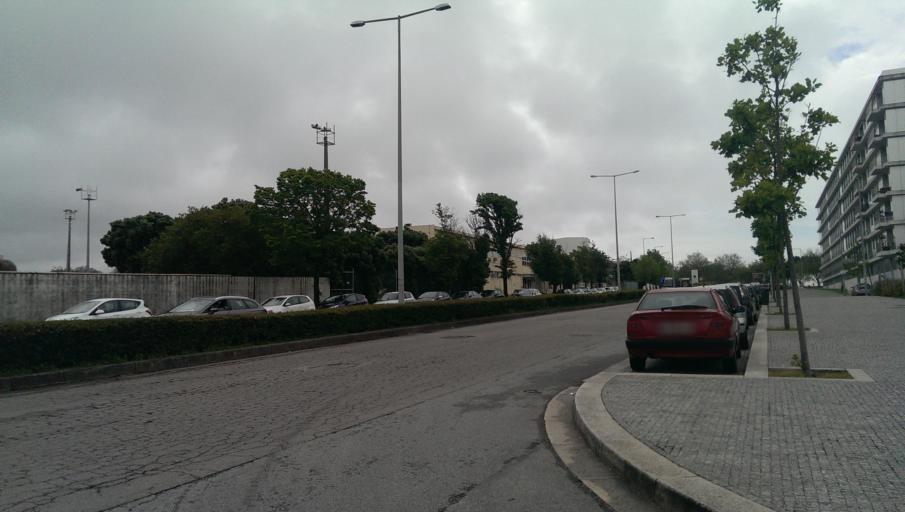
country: PT
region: Porto
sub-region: Matosinhos
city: Matosinhos
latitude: 41.1747
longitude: -8.6810
